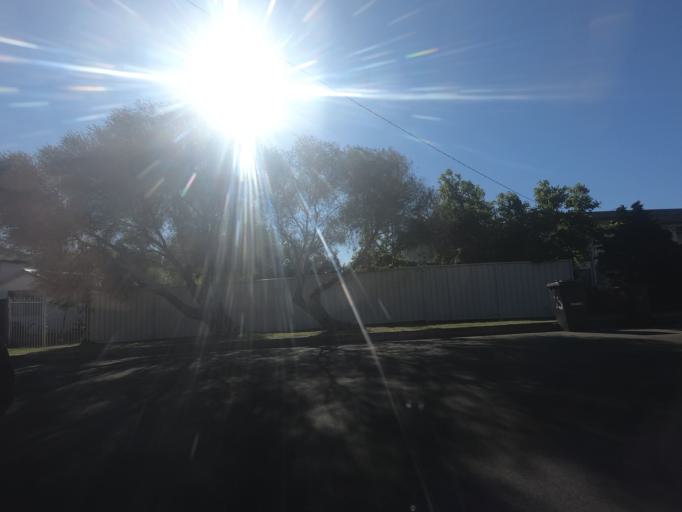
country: AU
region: New South Wales
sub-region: Wollongong
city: Corrimal
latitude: -34.3654
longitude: 150.8933
